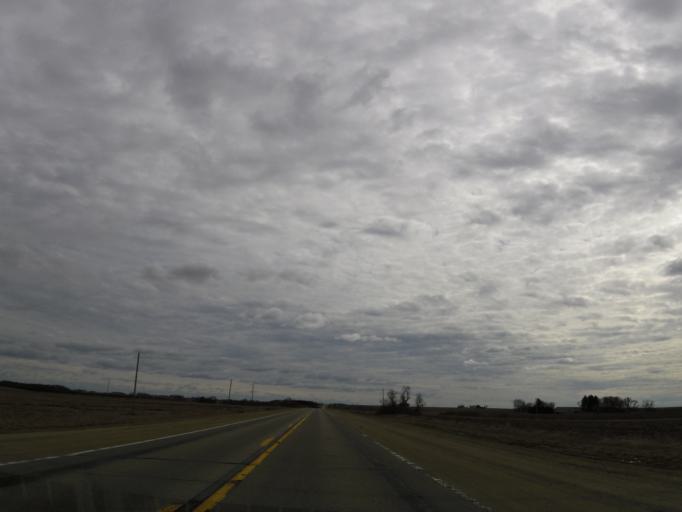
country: US
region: Iowa
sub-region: Howard County
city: Cresco
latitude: 43.4021
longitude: -92.2984
